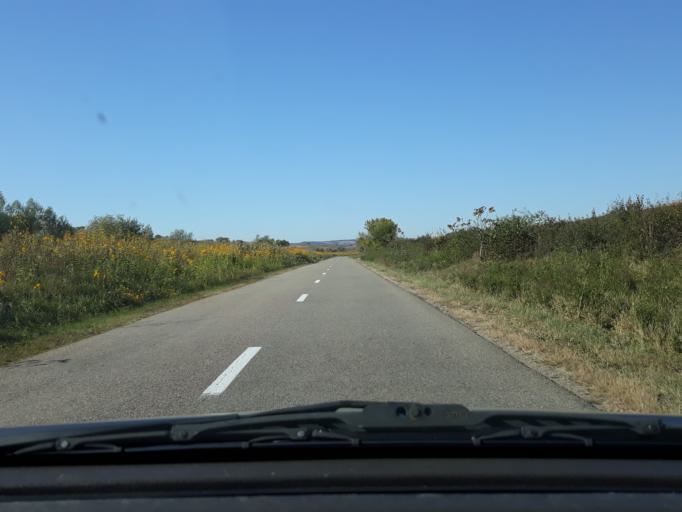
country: RO
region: Salaj
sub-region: Comuna Dobrin
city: Dobrin
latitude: 47.2960
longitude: 23.1185
